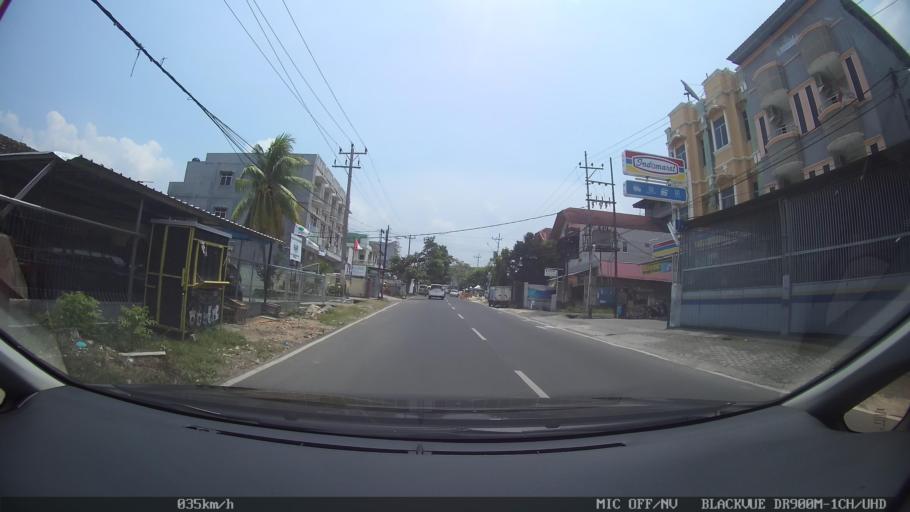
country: ID
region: Lampung
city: Bandarlampung
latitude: -5.4407
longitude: 105.2707
